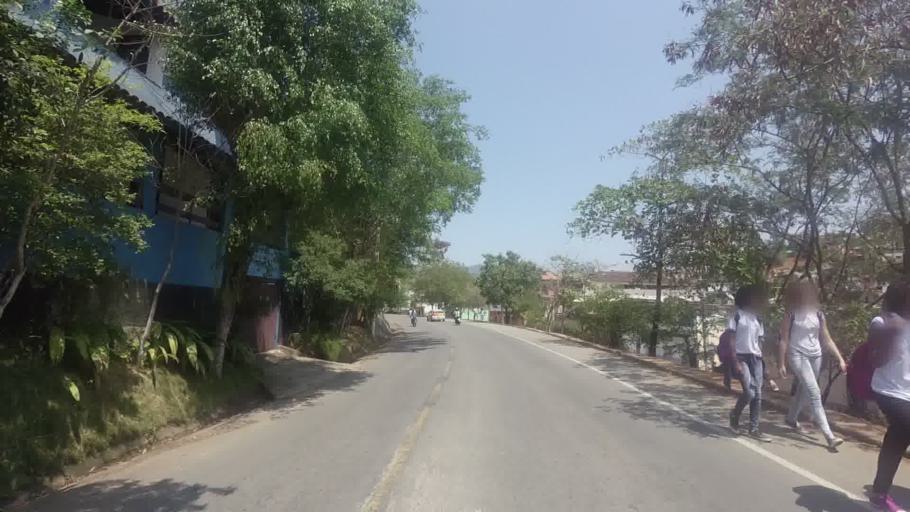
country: BR
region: Espirito Santo
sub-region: Cachoeiro De Itapemirim
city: Cachoeiro de Itapemirim
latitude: -20.8502
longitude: -41.1489
